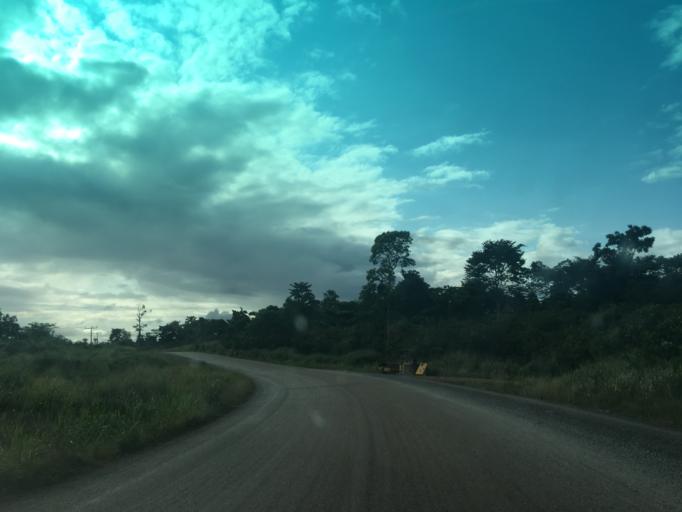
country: GH
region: Western
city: Bibiani
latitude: 6.1173
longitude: -2.3260
